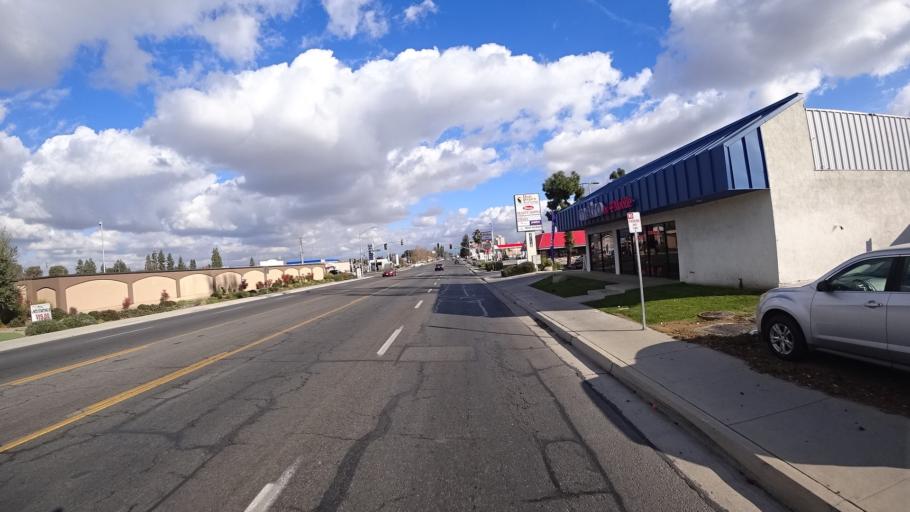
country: US
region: California
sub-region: Kern County
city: Bakersfield
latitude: 35.3322
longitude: -119.0444
